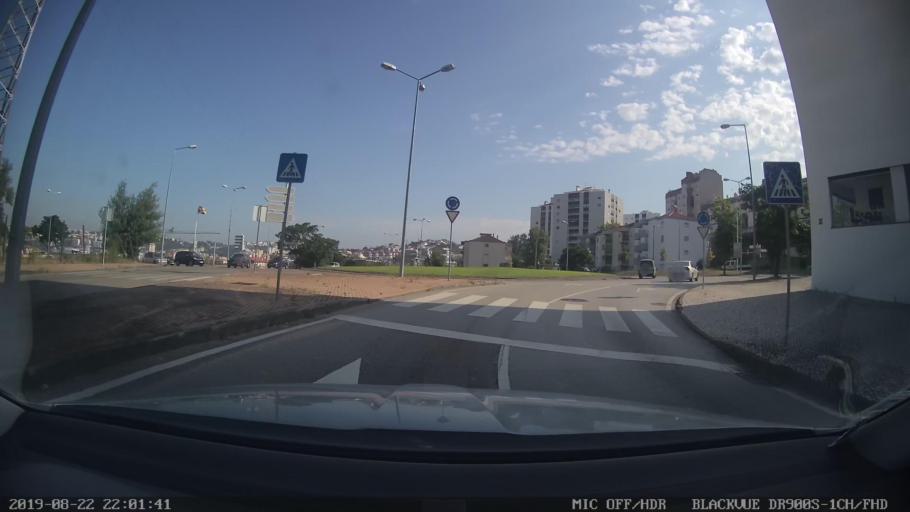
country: PT
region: Coimbra
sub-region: Coimbra
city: Coimbra
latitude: 40.1934
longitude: -8.3987
